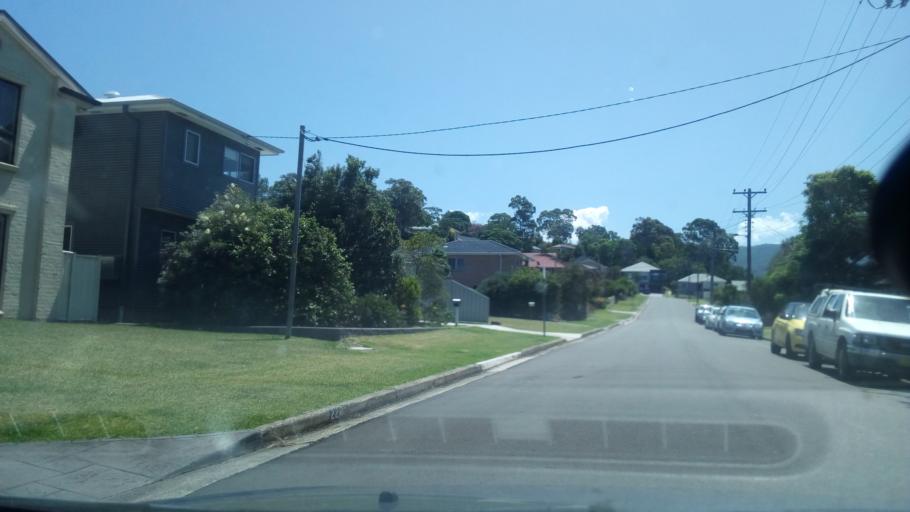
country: AU
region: New South Wales
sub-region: Wollongong
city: West Wollongong
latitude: -34.4330
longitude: 150.8613
